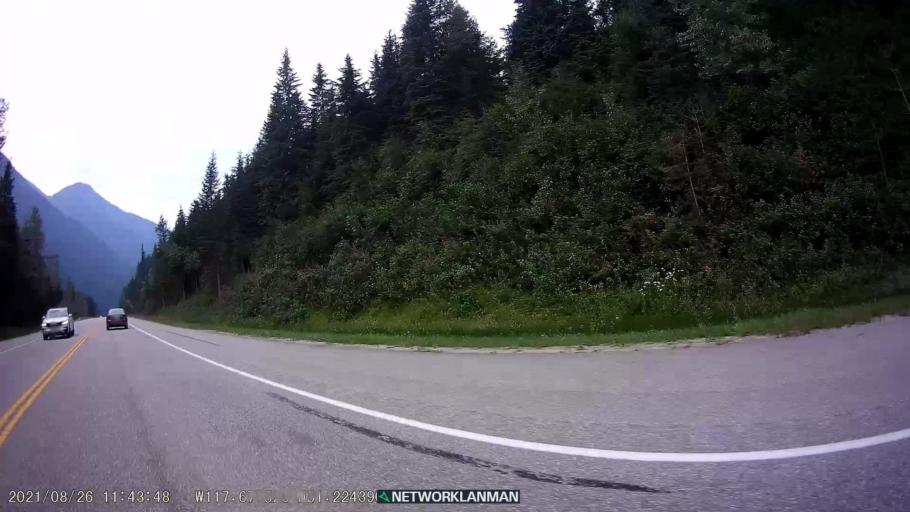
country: CA
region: British Columbia
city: Revelstoke
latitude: 51.2243
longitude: -117.6777
